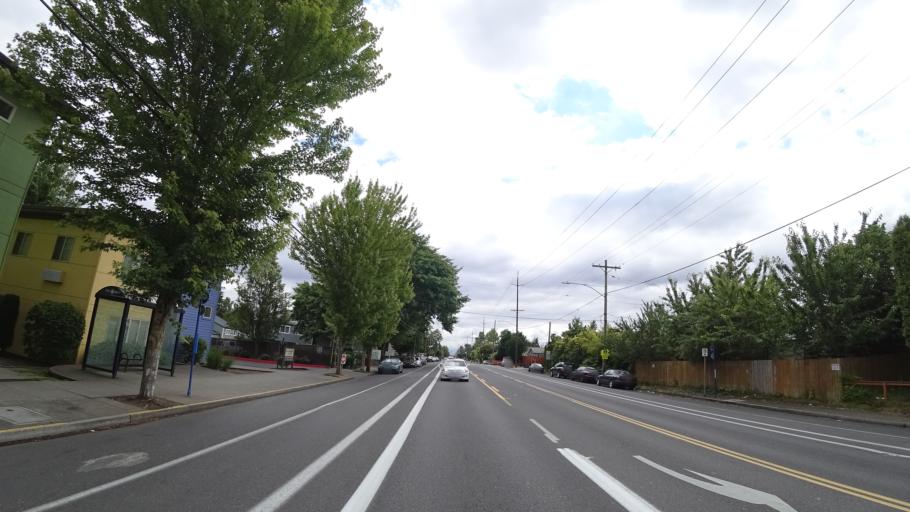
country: US
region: Oregon
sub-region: Multnomah County
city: Portland
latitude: 45.5628
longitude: -122.6095
